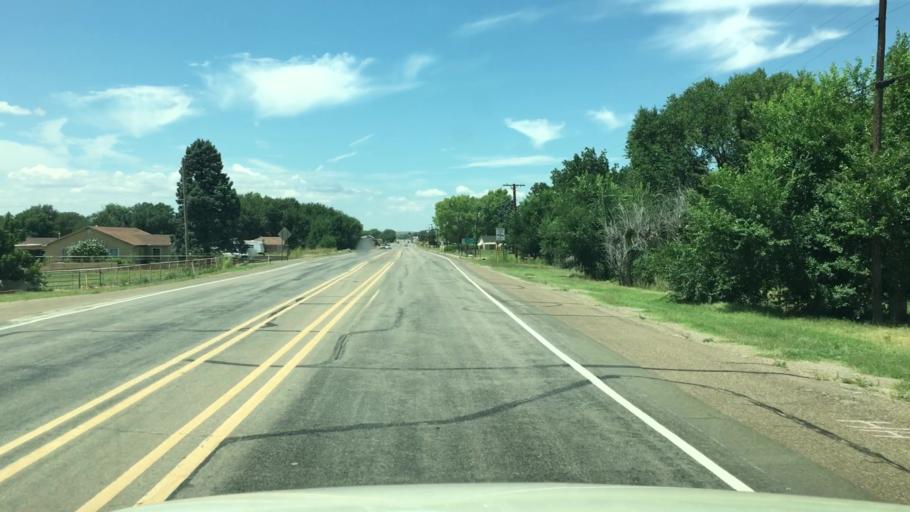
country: US
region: New Mexico
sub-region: De Baca County
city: Fort Sumner
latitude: 34.4646
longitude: -104.2233
